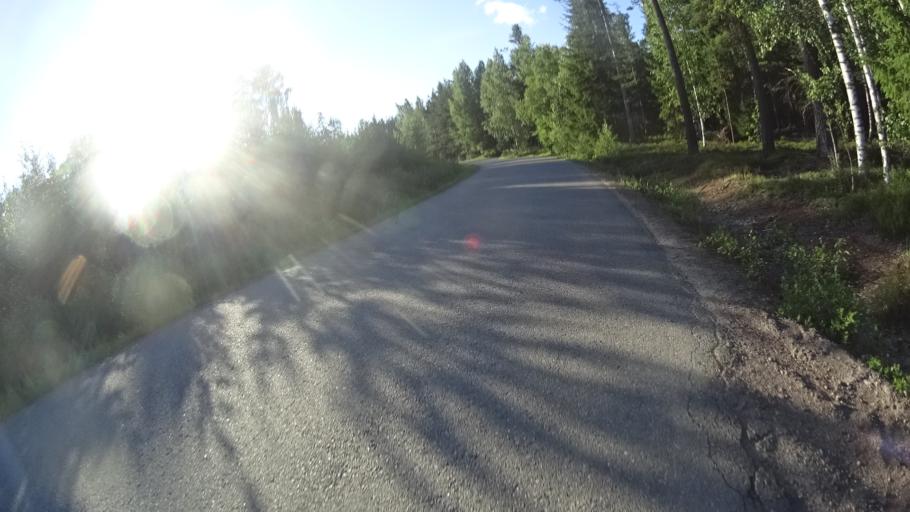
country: FI
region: Uusimaa
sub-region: Helsinki
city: Karkkila
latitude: 60.5953
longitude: 24.1214
